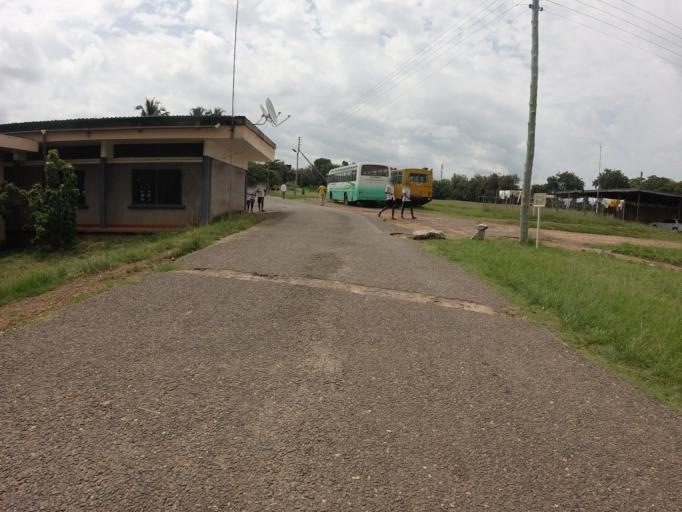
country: GH
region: Volta
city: Ho
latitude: 6.5973
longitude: 0.4751
